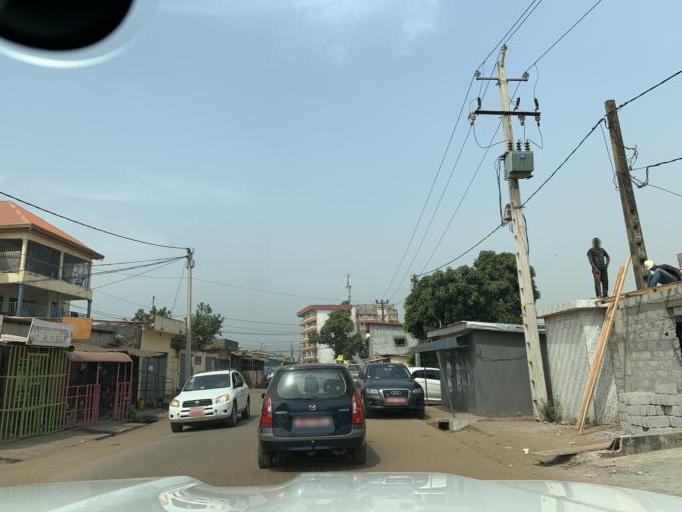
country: GN
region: Conakry
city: Conakry
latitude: 9.5539
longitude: -13.6682
